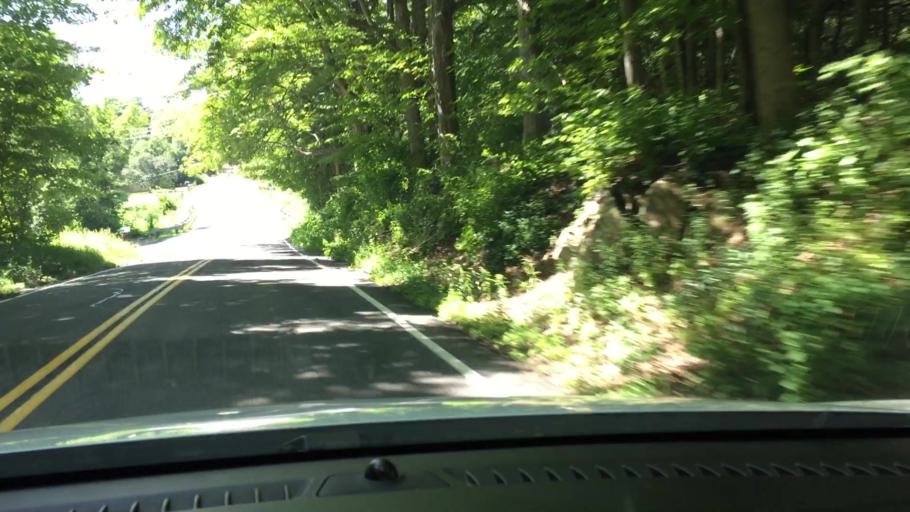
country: US
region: Massachusetts
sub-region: Berkshire County
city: Pittsfield
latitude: 42.4044
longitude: -73.2536
